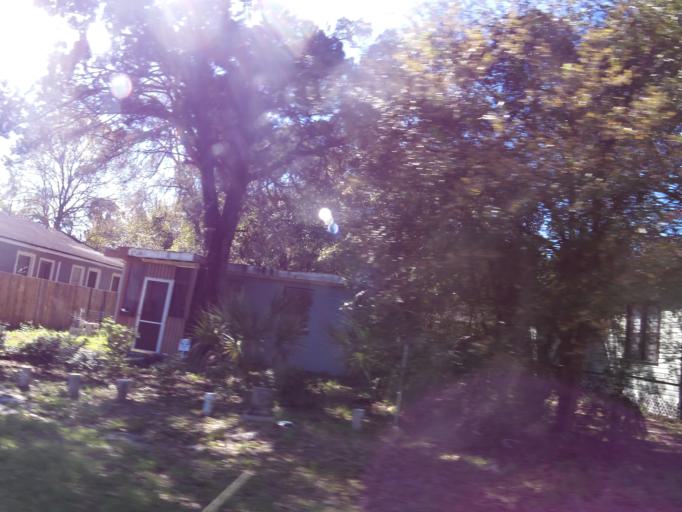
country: US
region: Florida
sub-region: Duval County
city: Jacksonville
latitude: 30.3615
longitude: -81.6432
